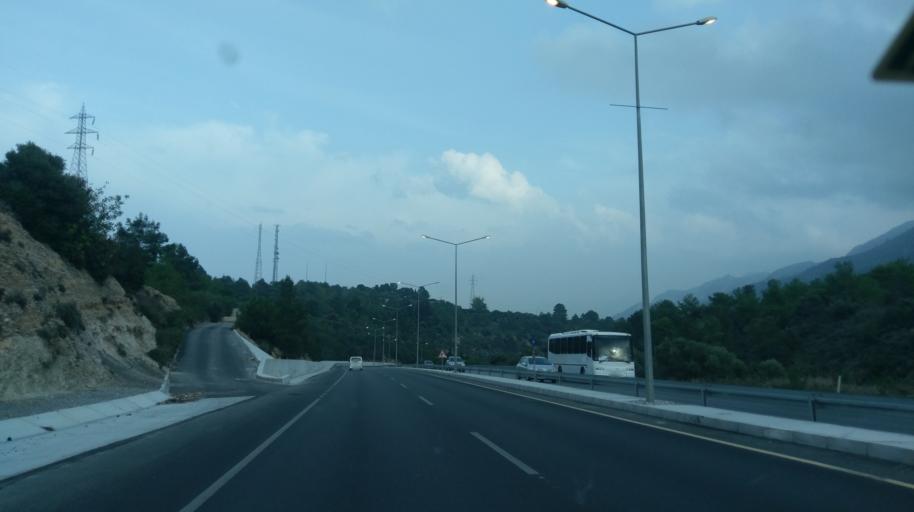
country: CY
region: Keryneia
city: Kyrenia
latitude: 35.3093
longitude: 33.3131
